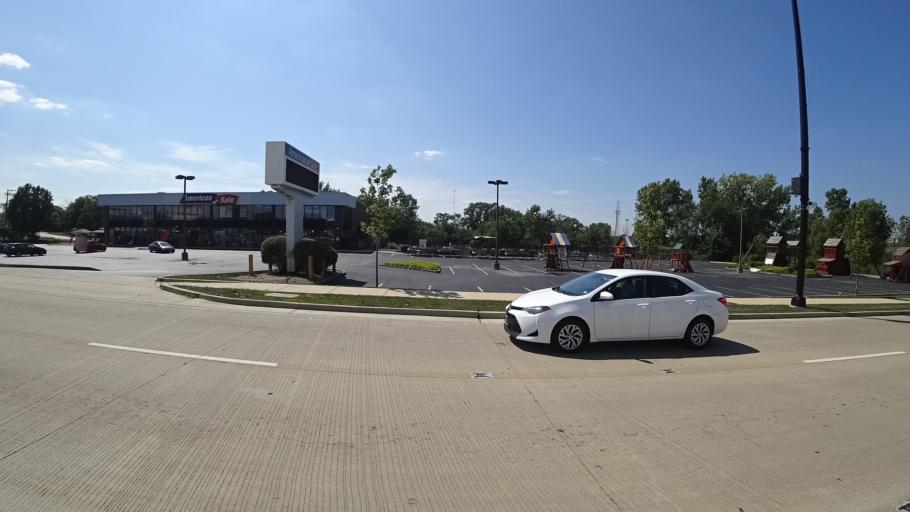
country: US
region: Illinois
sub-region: Cook County
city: Orland Hills
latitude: 41.5879
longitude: -87.8523
